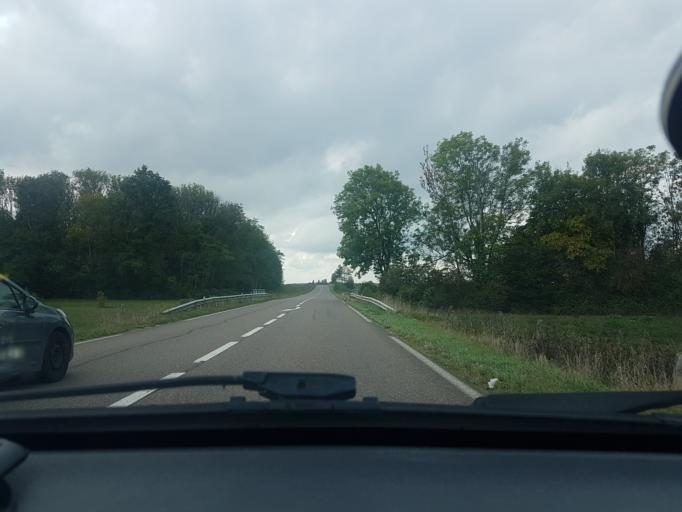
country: FR
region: Franche-Comte
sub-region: Departement de la Haute-Saone
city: Villersexel
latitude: 47.5434
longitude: 6.5010
